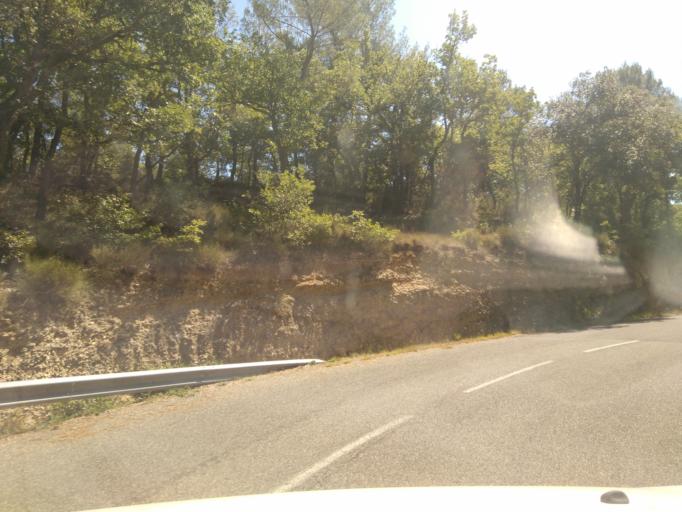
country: FR
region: Provence-Alpes-Cote d'Azur
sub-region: Departement du Var
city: Regusse
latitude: 43.7140
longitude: 6.0473
